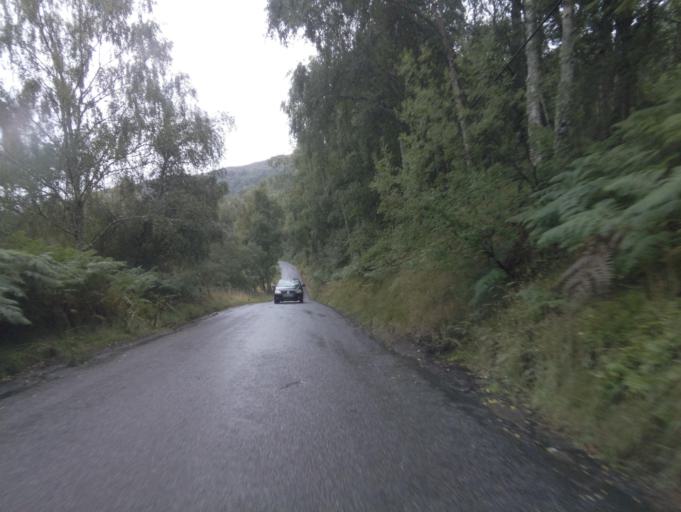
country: GB
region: Scotland
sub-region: Aberdeenshire
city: Ballater
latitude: 57.0778
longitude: -3.0876
